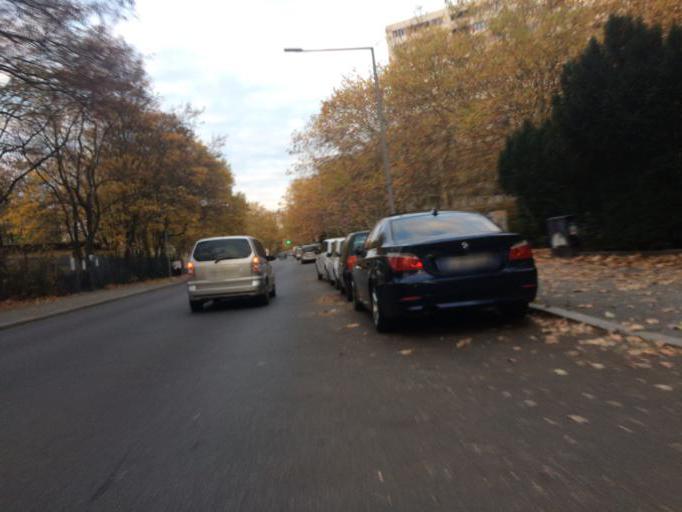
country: DE
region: Berlin
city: Markisches Viertel
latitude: 52.6006
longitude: 13.3568
